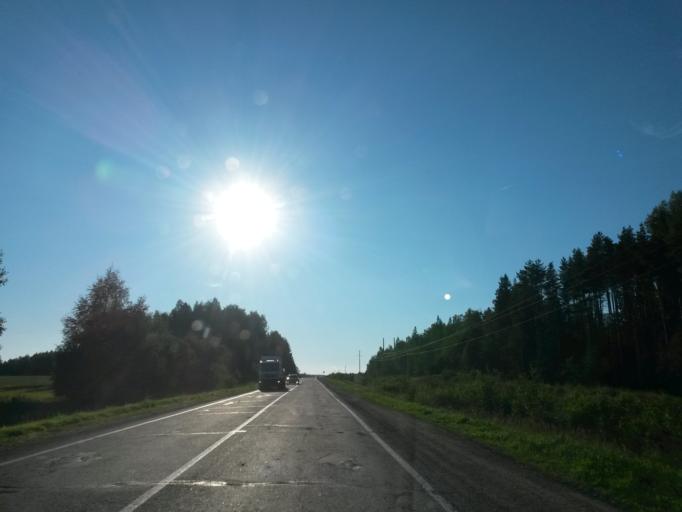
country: RU
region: Jaroslavl
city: Gavrilov-Yam
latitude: 57.2608
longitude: 40.0502
